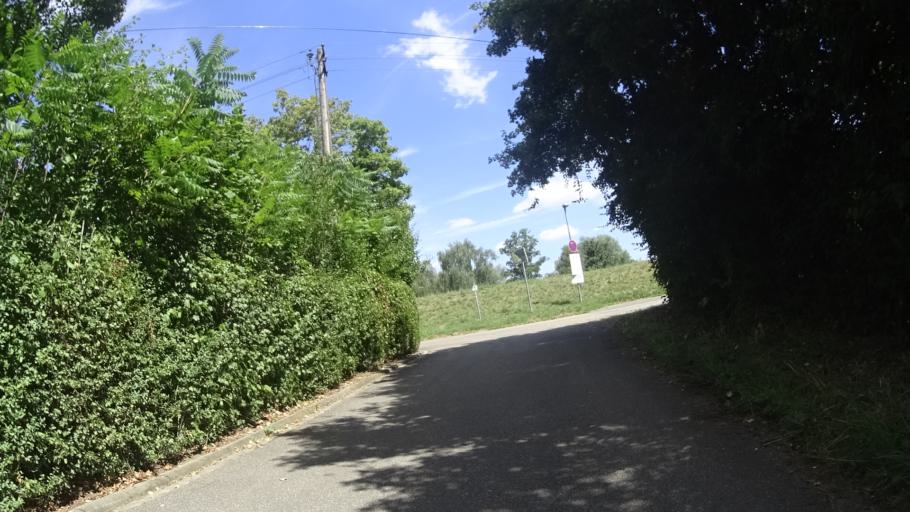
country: DE
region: Baden-Wuerttemberg
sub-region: Karlsruhe Region
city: Ketsch
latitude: 49.3558
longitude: 8.5183
